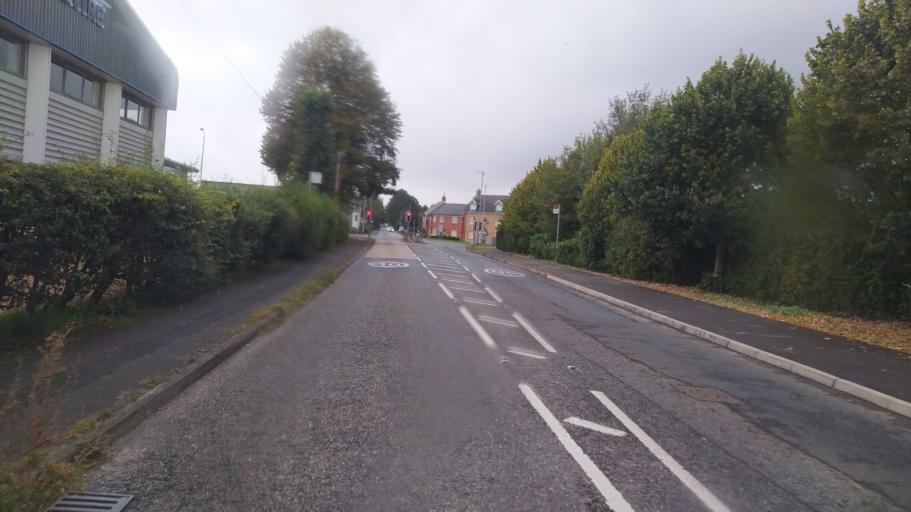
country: GB
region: England
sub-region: Wiltshire
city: Salisbury
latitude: 51.1039
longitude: -1.7794
